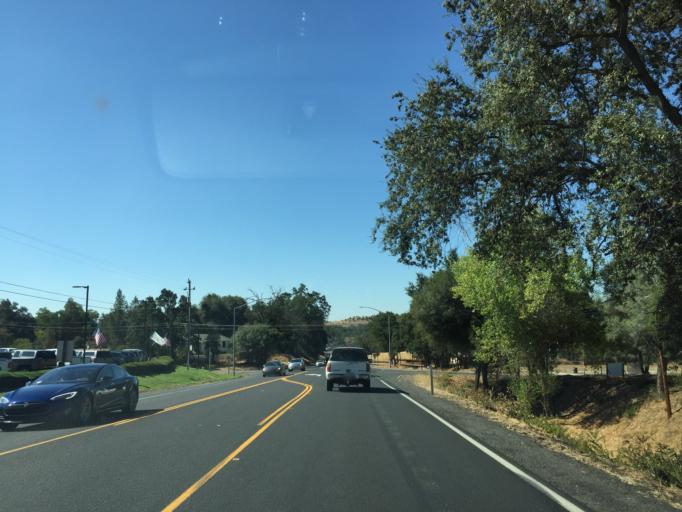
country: US
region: California
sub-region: Tuolumne County
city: Jamestown
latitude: 37.9589
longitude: -120.4173
